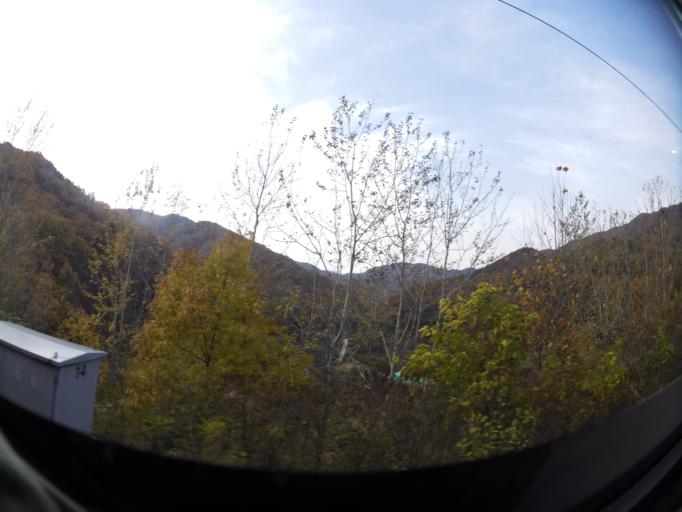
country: KR
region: Gyeongsangbuk-do
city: Gimcheon
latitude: 36.1654
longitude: 128.0071
